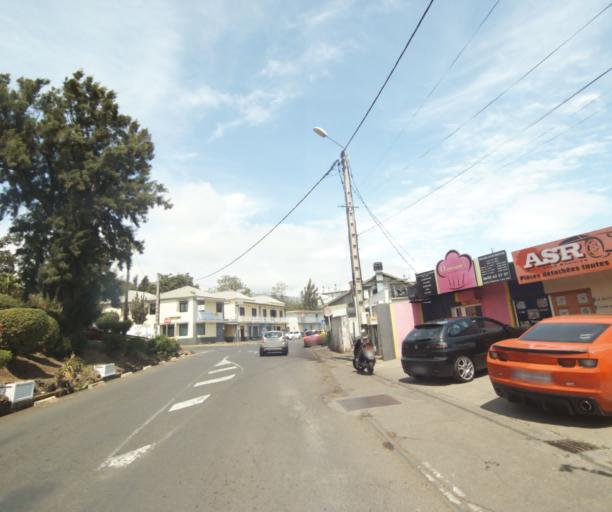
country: RE
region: Reunion
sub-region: Reunion
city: Trois-Bassins
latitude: -21.0803
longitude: 55.2705
